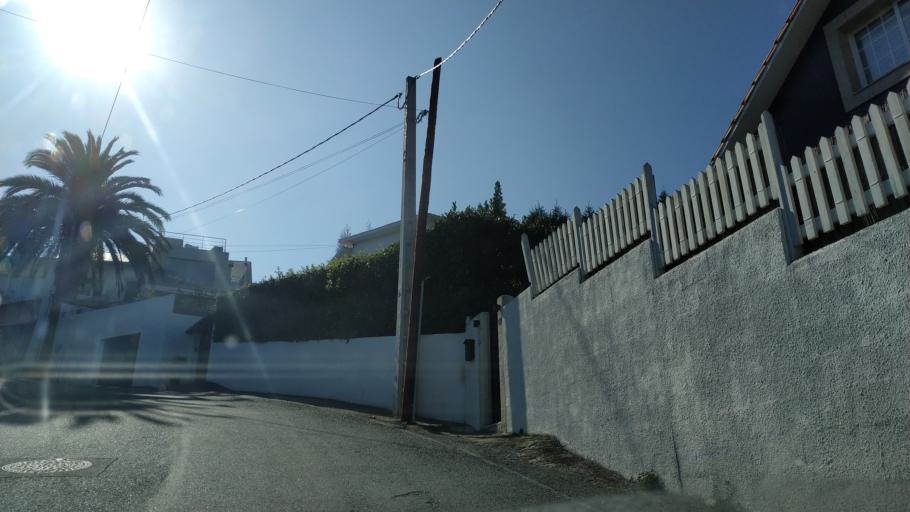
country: ES
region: Galicia
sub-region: Provincia da Coruna
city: Culleredo
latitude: 43.3251
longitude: -8.3880
